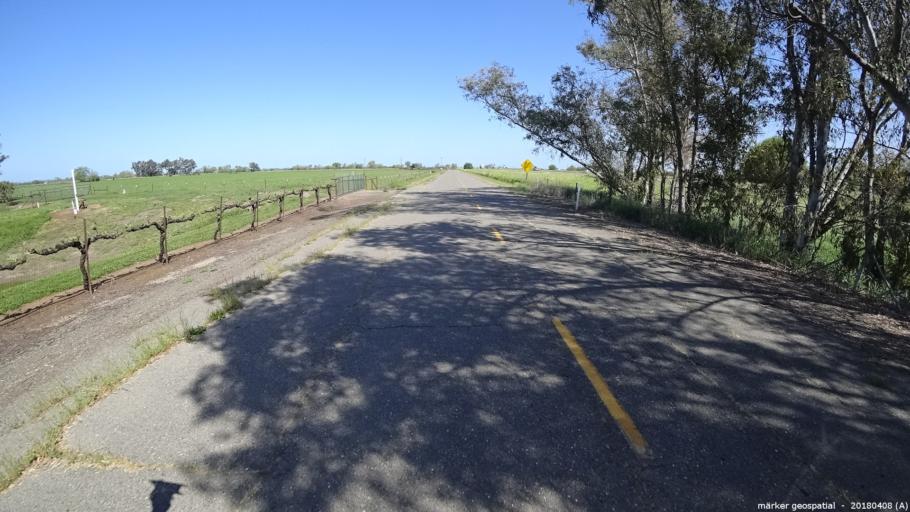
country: US
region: California
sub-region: Sacramento County
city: Laguna
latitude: 38.3361
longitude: -121.4693
